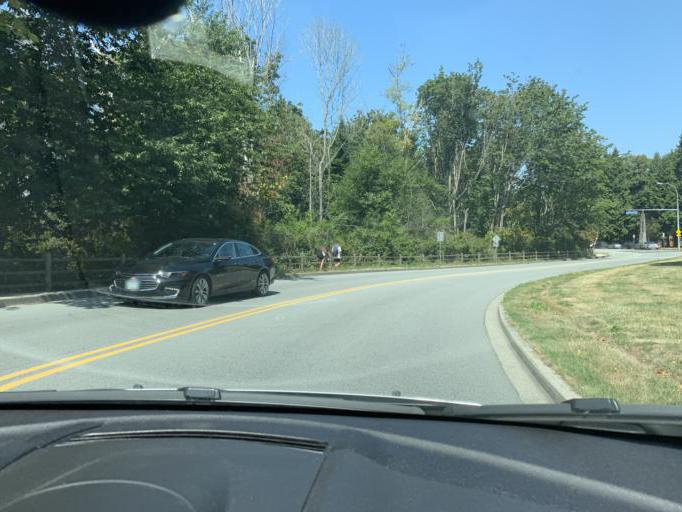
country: CA
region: British Columbia
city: West End
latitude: 49.2620
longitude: -123.2585
